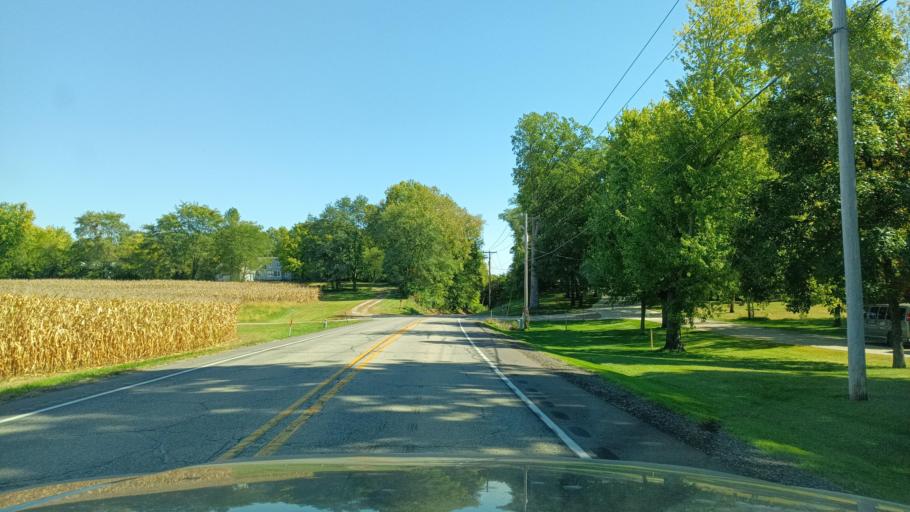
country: US
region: Illinois
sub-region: Woodford County
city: Eureka
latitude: 40.6274
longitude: -89.2541
